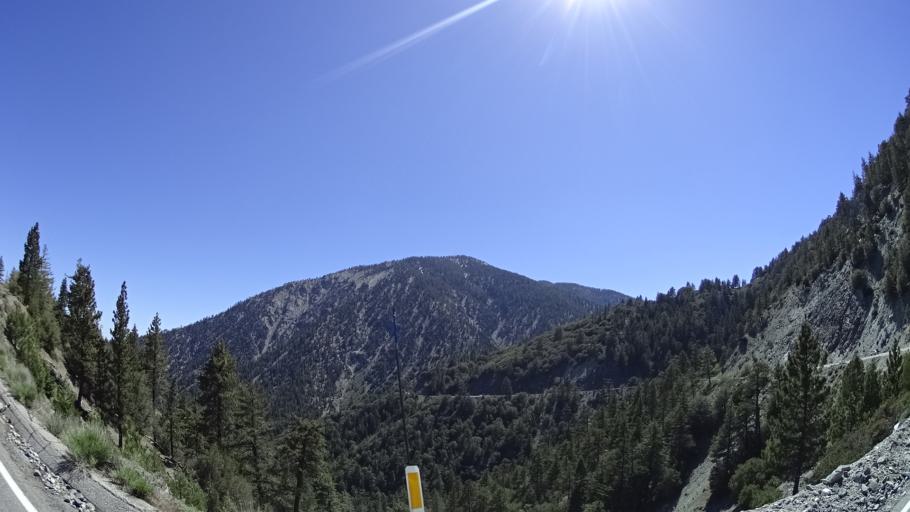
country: US
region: California
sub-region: San Bernardino County
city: Wrightwood
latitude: 34.3781
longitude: -117.7416
